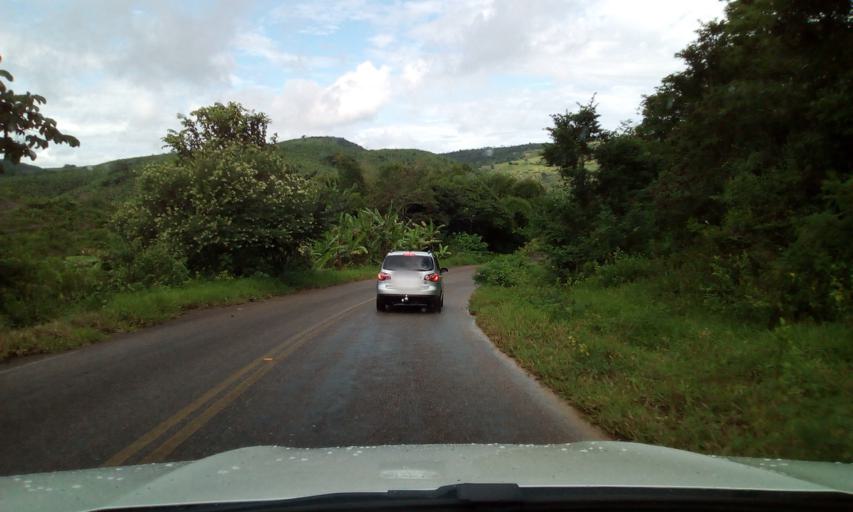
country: BR
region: Paraiba
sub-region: Areia
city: Areia
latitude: -6.9199
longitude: -35.6389
